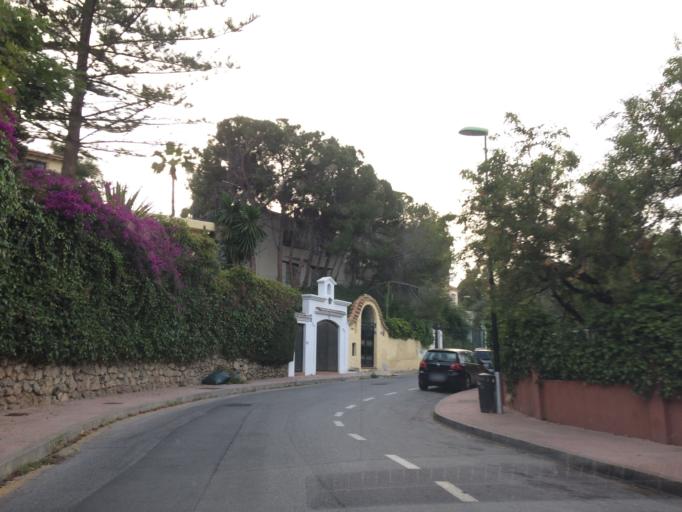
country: ES
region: Andalusia
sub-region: Provincia de Malaga
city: Malaga
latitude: 36.7300
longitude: -4.3842
